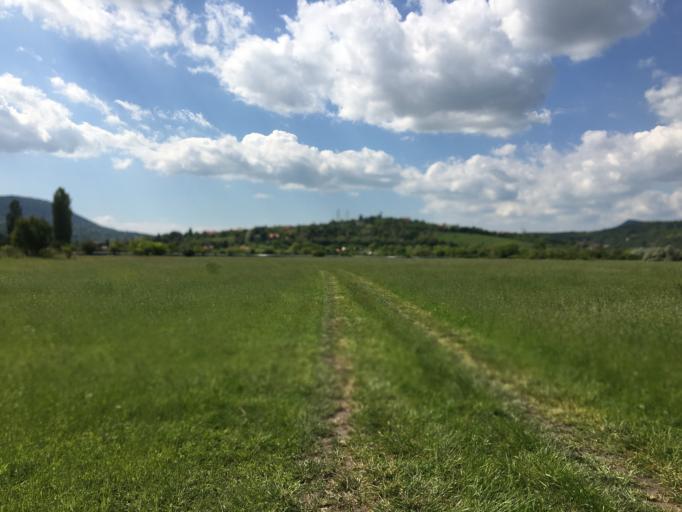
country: HU
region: Budapest
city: Budapest III. keruelet
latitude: 47.5706
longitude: 19.0376
